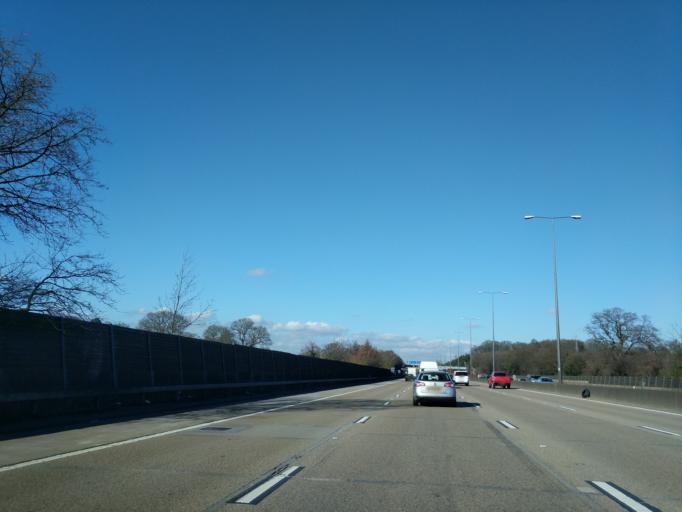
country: GB
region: England
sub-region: Surrey
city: Addlestone
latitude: 51.3585
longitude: -0.4956
